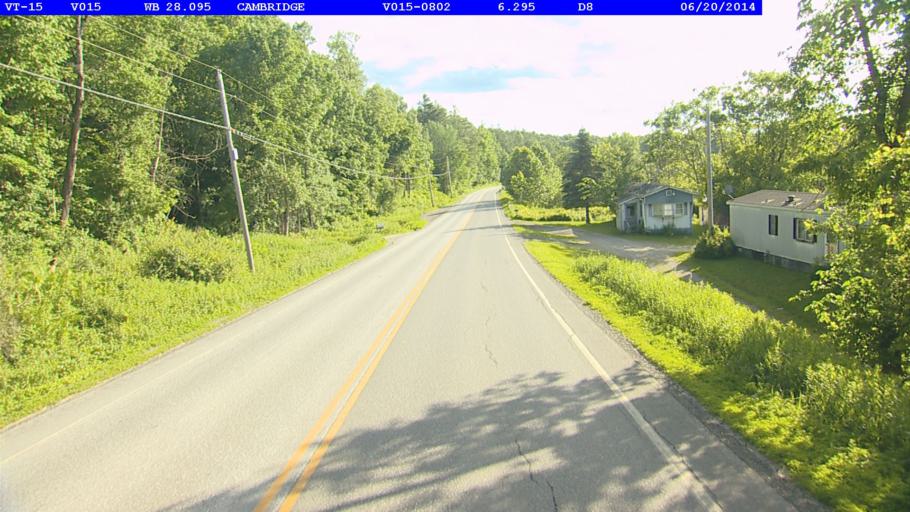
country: US
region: Vermont
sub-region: Lamoille County
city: Johnson
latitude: 44.6513
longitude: -72.8075
